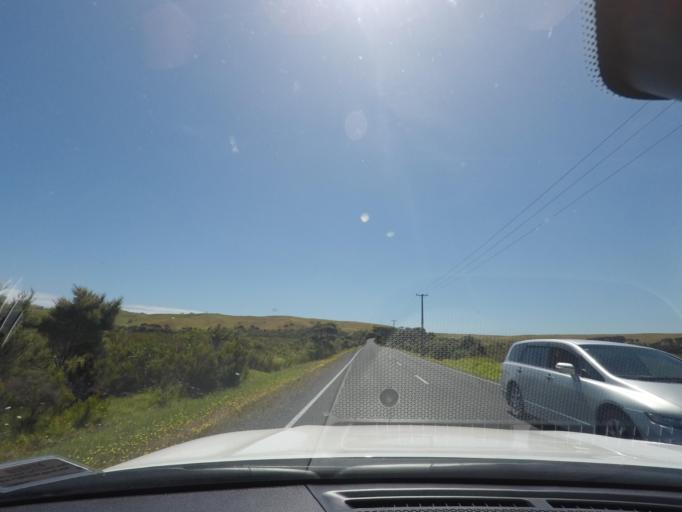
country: NZ
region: Auckland
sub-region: Auckland
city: Parakai
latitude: -36.6292
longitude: 174.3678
